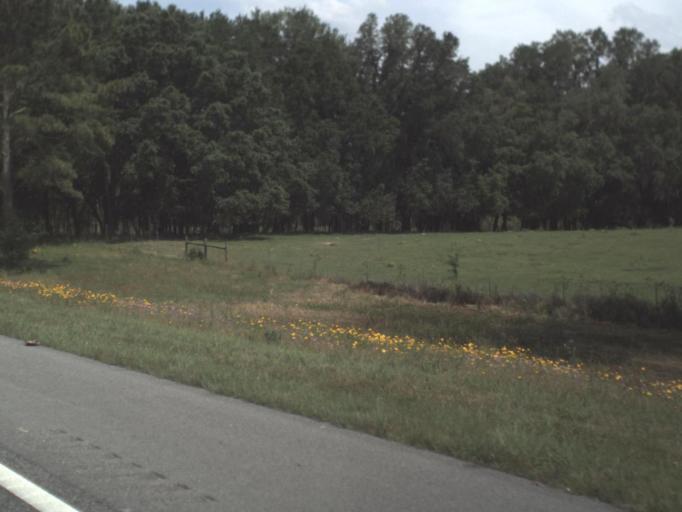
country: US
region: Florida
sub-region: Suwannee County
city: Live Oak
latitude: 30.3509
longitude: -83.0450
